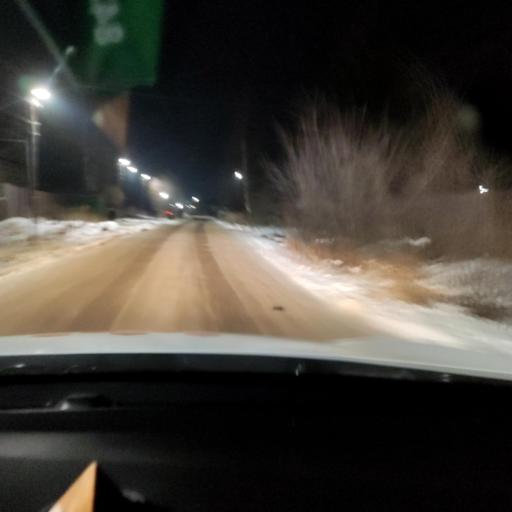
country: RU
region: Tatarstan
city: Stolbishchi
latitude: 55.6506
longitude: 49.2127
